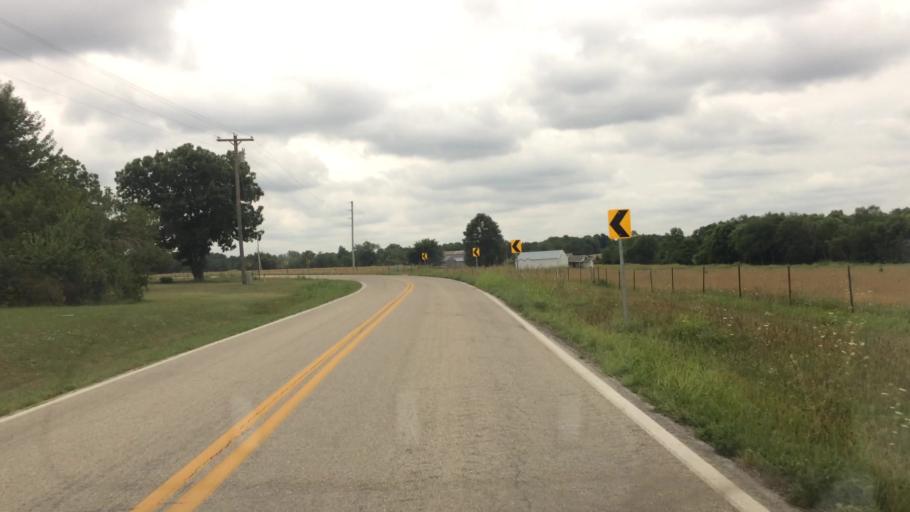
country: US
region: Missouri
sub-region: Greene County
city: Strafford
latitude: 37.2972
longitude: -93.1204
